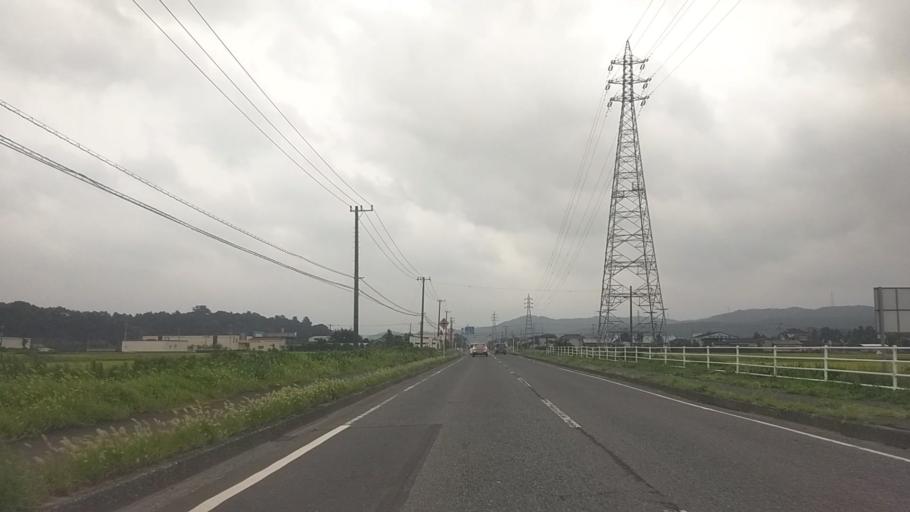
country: JP
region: Chiba
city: Kisarazu
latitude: 35.3277
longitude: 140.0550
